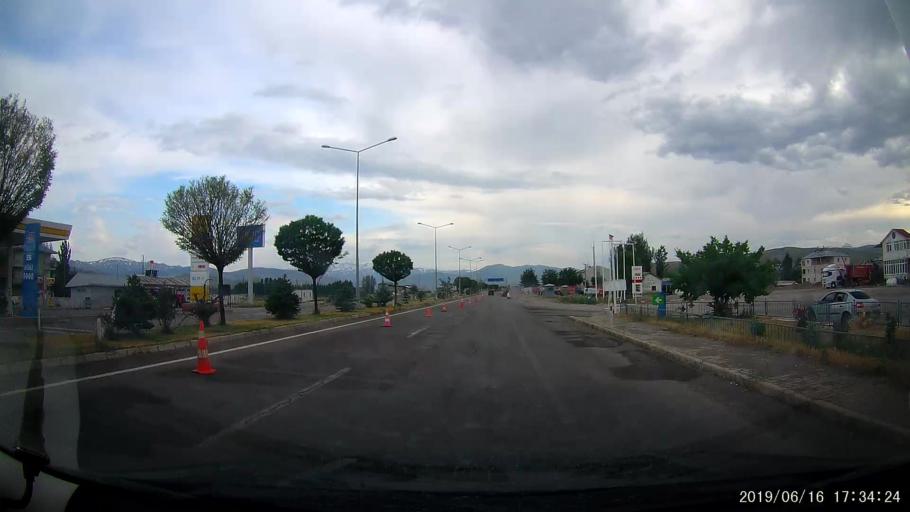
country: TR
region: Erzincan
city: Tercan
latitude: 39.7415
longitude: 40.2688
